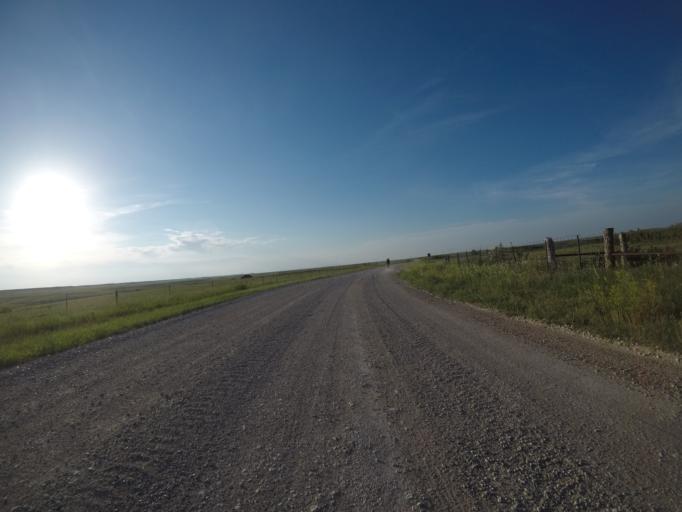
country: US
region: Kansas
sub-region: Riley County
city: Manhattan
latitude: 39.0435
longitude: -96.4933
